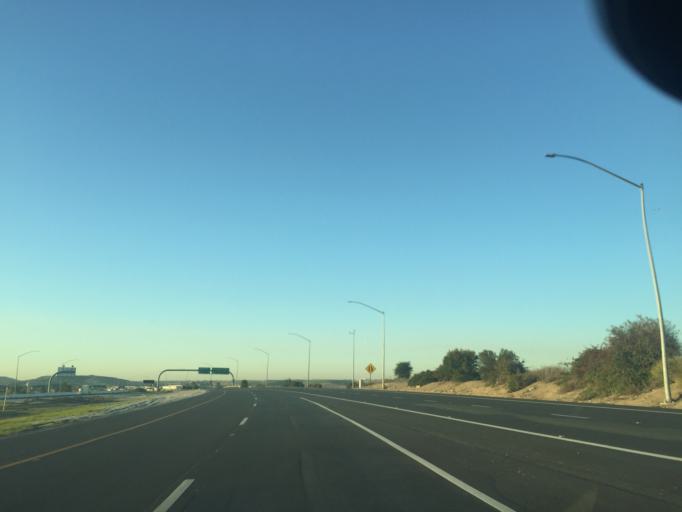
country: MX
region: Baja California
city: Tijuana
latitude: 32.5711
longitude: -116.9499
